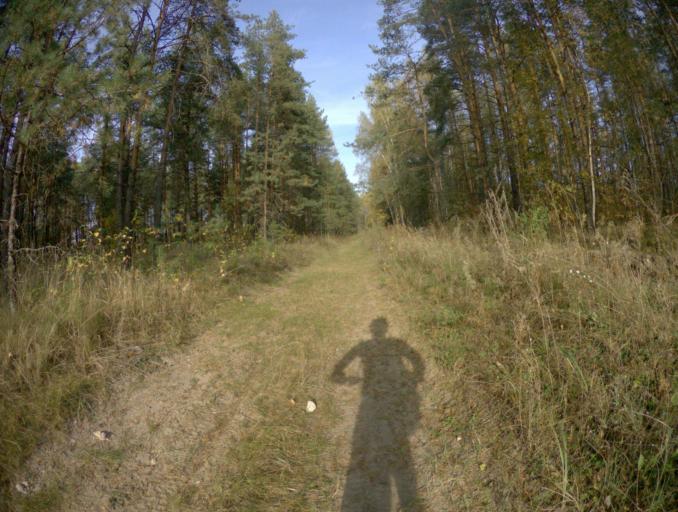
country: RU
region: Vladimir
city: Sobinka
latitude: 55.9416
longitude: 40.0523
